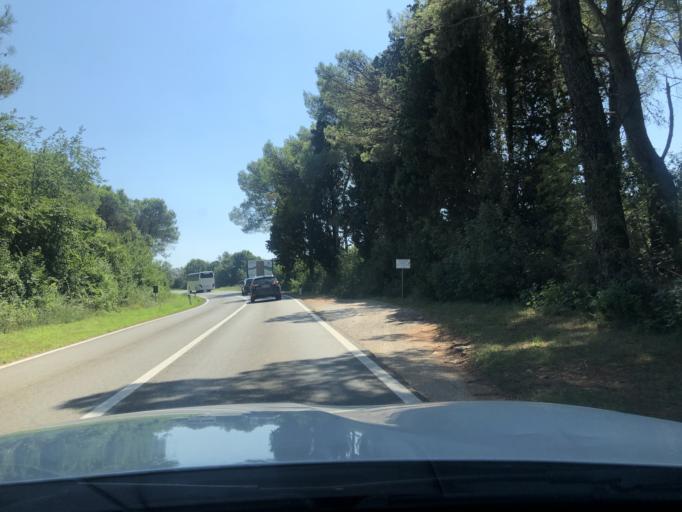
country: HR
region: Istarska
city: Vodnjan
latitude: 45.0321
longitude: 13.7928
